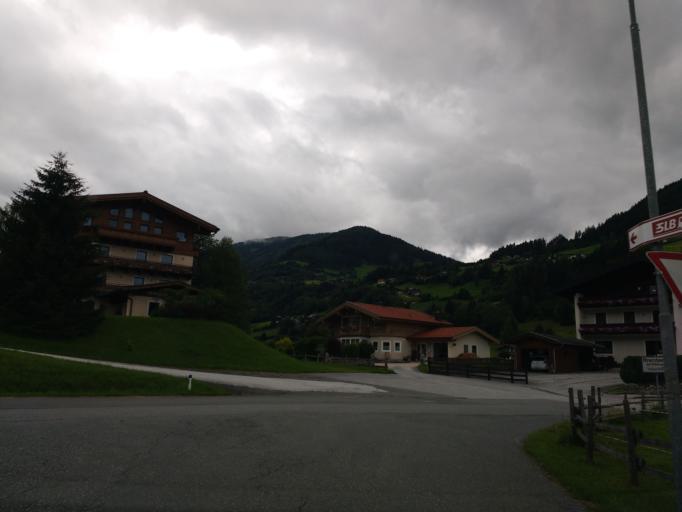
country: AT
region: Salzburg
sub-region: Politischer Bezirk Zell am See
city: Hollersbach im Pinzgau
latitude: 47.2790
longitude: 12.3870
